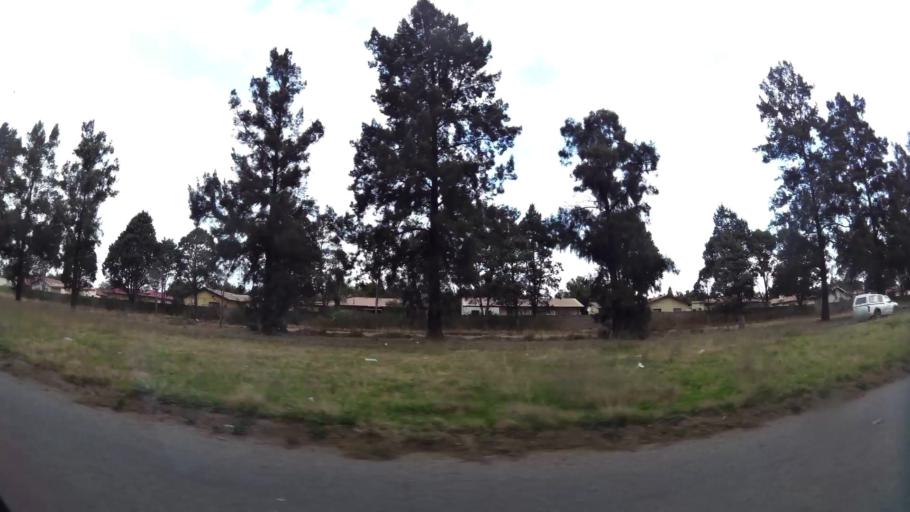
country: ZA
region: Gauteng
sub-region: Sedibeng District Municipality
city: Vanderbijlpark
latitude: -26.6739
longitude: 27.8351
